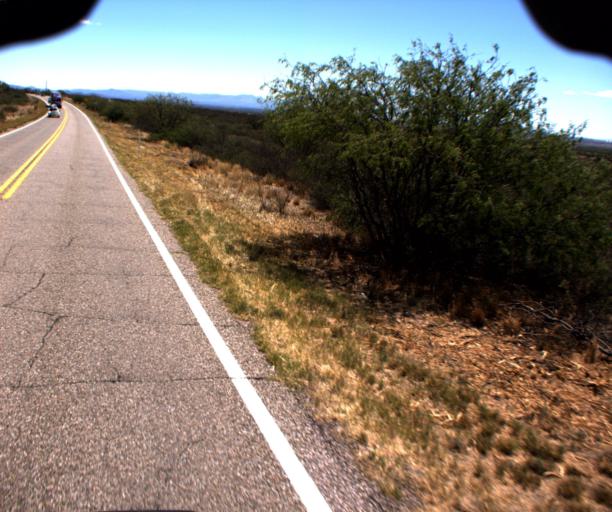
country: US
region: Arizona
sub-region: Cochise County
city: Huachuca City
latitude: 31.6923
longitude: -110.4045
